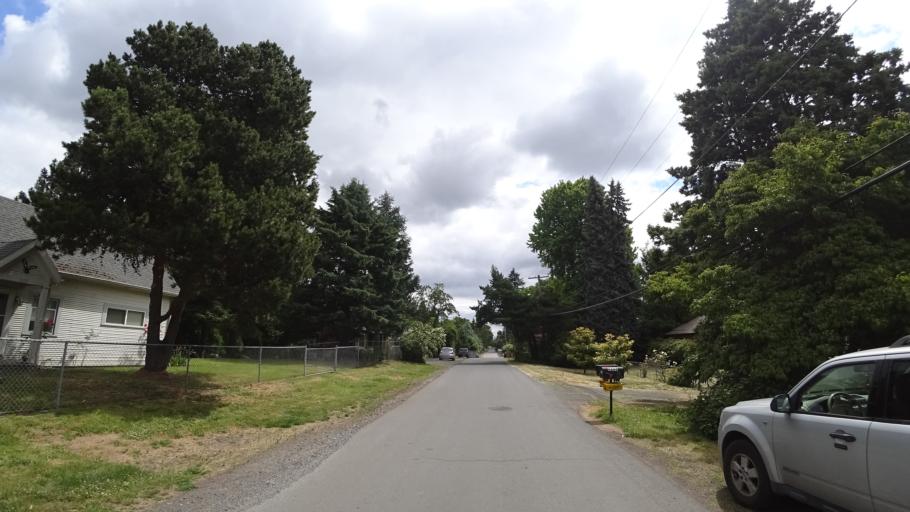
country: US
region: Oregon
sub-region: Multnomah County
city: Portland
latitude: 45.5651
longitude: -122.6144
